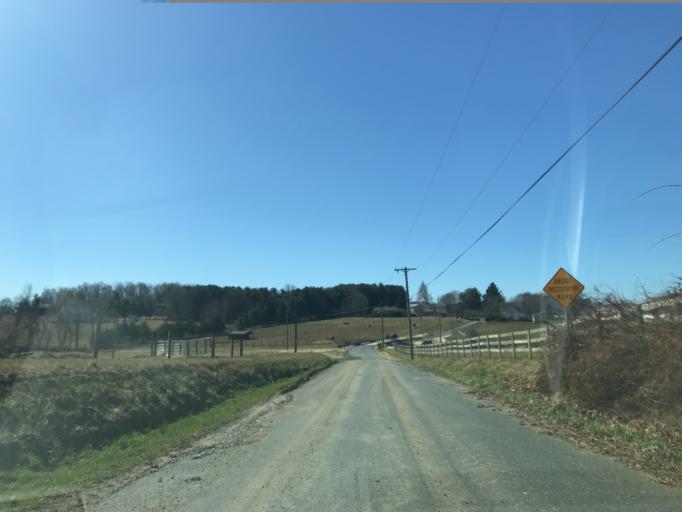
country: US
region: Pennsylvania
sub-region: York County
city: Stewartstown
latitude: 39.7156
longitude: -76.5250
